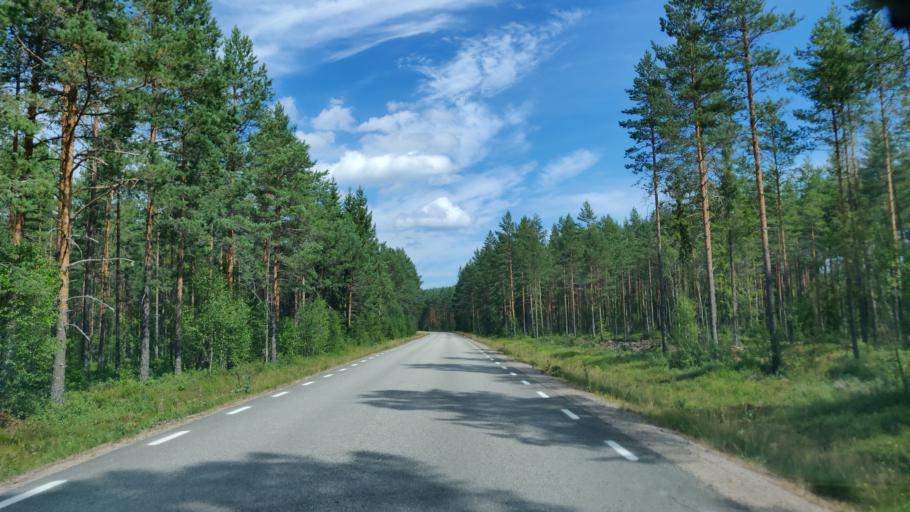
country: SE
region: Vaermland
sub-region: Hagfors Kommun
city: Ekshaerad
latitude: 60.0827
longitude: 13.5034
